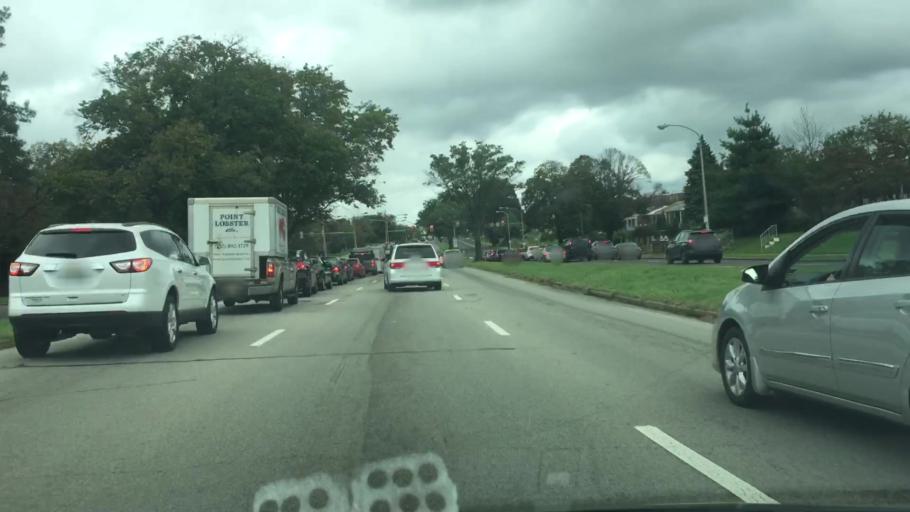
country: US
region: Pennsylvania
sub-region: Montgomery County
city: Rockledge
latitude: 40.0699
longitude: -75.0391
